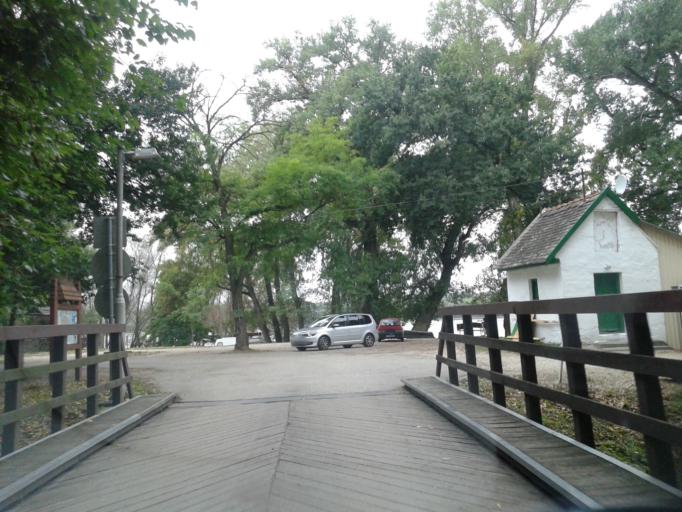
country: HU
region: Bacs-Kiskun
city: Harta
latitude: 46.6927
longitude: 19.0108
